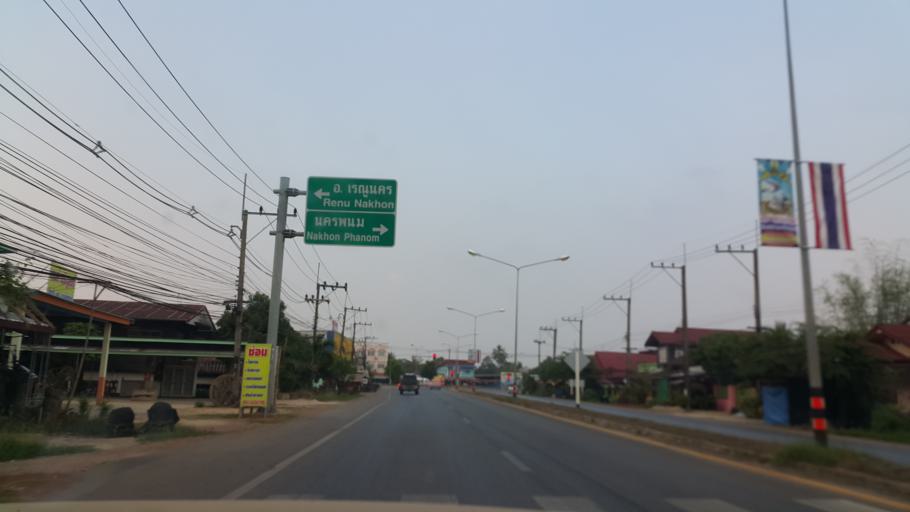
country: TH
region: Nakhon Phanom
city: Renu Nakhon
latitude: 17.0166
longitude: 104.7264
